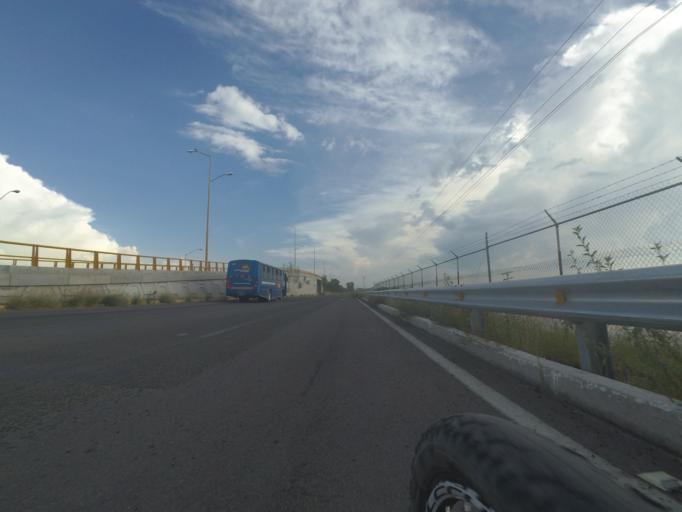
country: MX
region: Aguascalientes
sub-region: Aguascalientes
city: Penuelas (El Cienegal)
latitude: 21.7188
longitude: -102.3104
